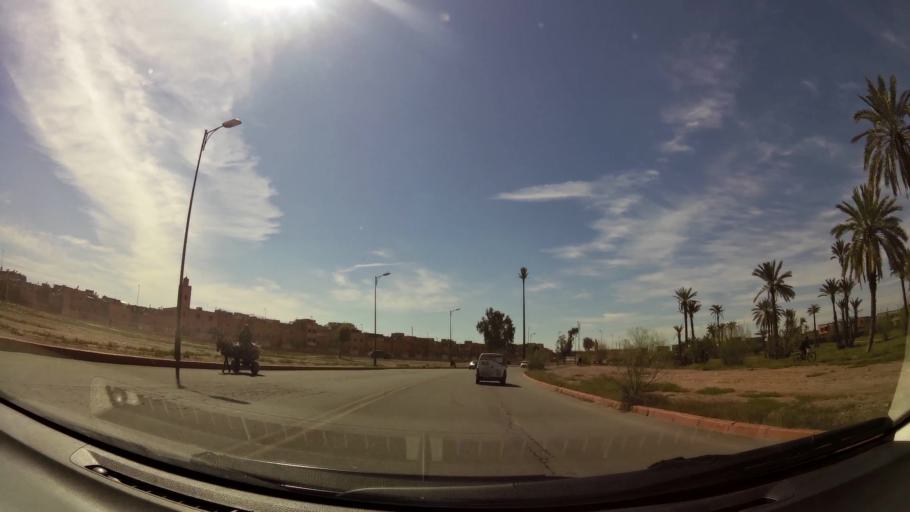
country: MA
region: Marrakech-Tensift-Al Haouz
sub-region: Marrakech
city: Marrakesh
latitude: 31.6209
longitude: -7.9661
